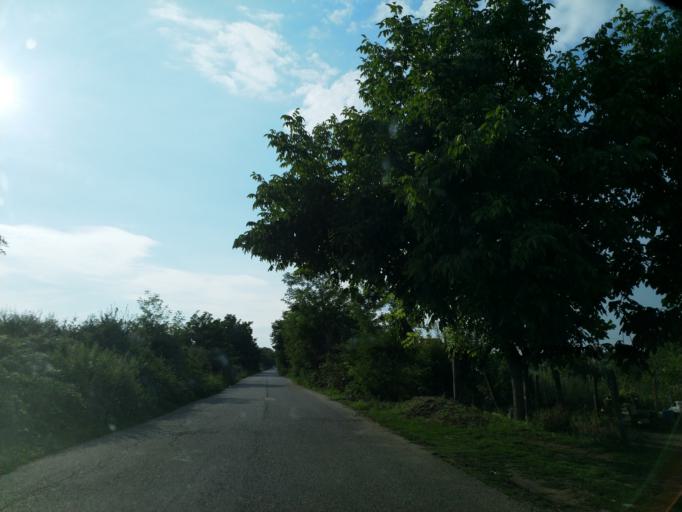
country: RS
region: Central Serbia
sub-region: Pomoravski Okrug
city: Jagodina
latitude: 43.9800
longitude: 21.2283
